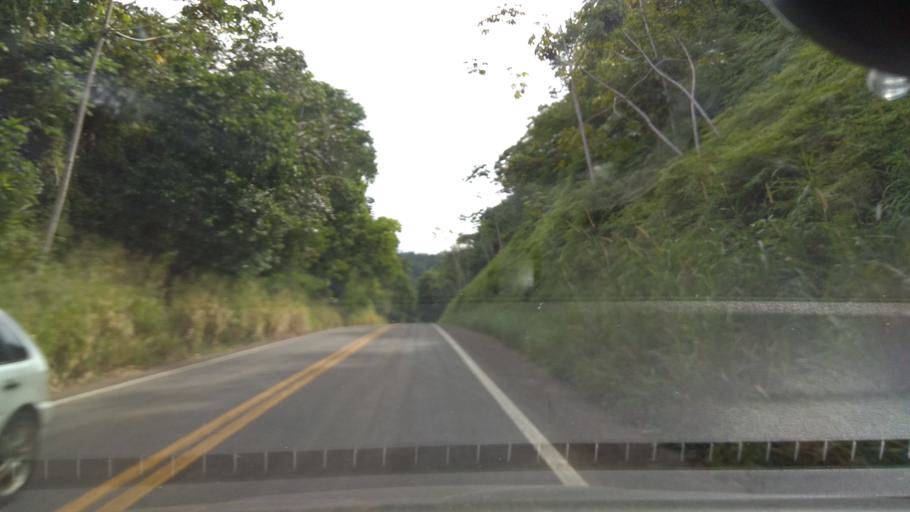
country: BR
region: Bahia
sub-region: Ubata
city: Ubata
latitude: -14.2272
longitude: -39.4744
